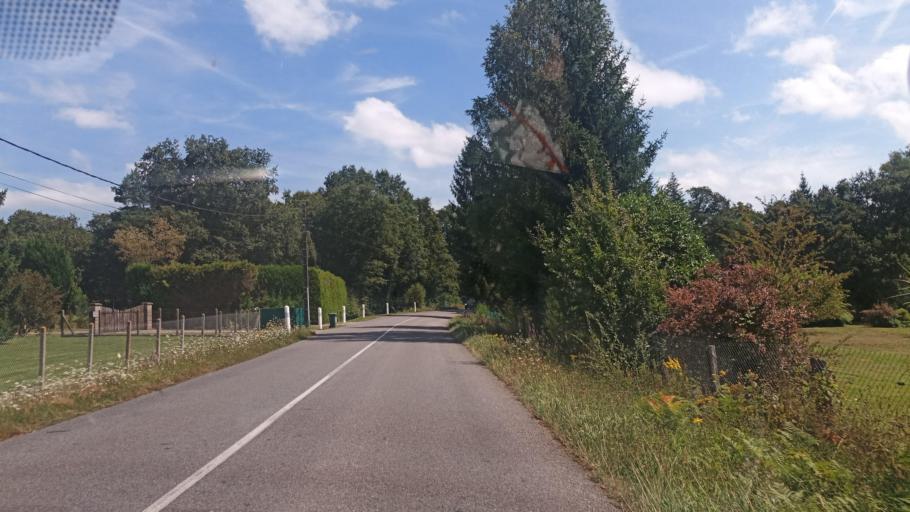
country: FR
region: Limousin
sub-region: Departement de la Haute-Vienne
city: Veyrac
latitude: 45.9032
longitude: 1.0775
